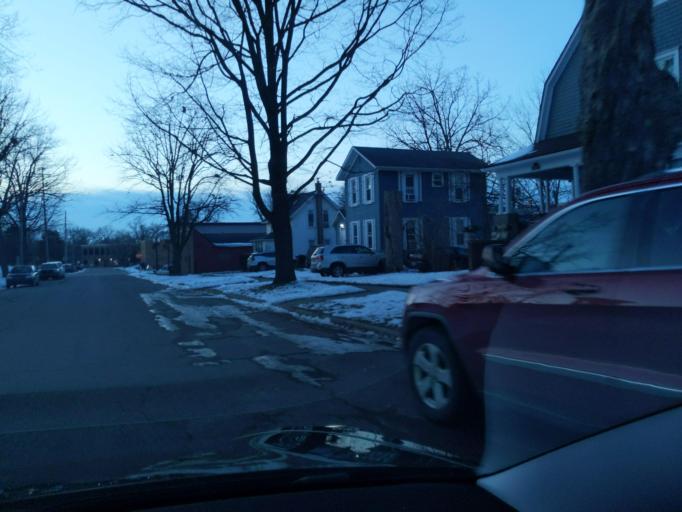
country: US
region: Michigan
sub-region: Ingham County
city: Mason
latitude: 42.5782
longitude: -84.4420
